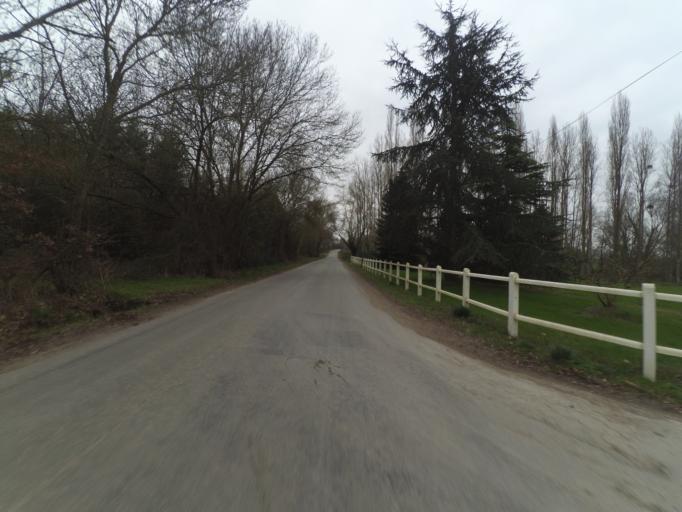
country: FR
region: Pays de la Loire
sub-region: Departement de la Loire-Atlantique
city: Coueron
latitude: 47.2488
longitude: -1.7066
